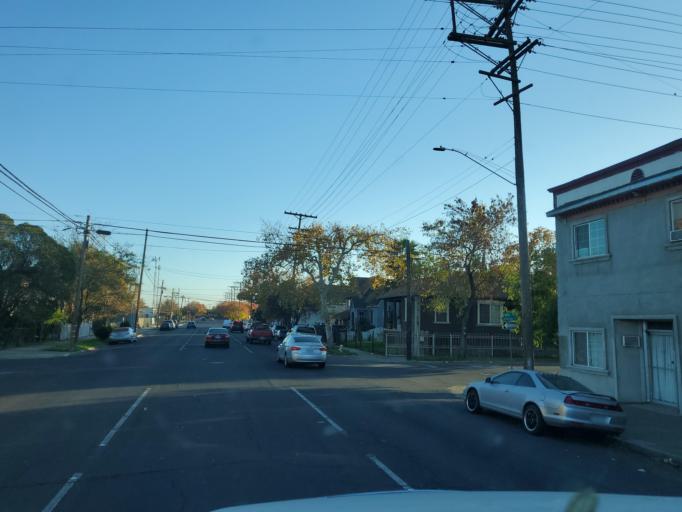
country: US
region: California
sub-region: San Joaquin County
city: Stockton
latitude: 37.9418
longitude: -121.2882
